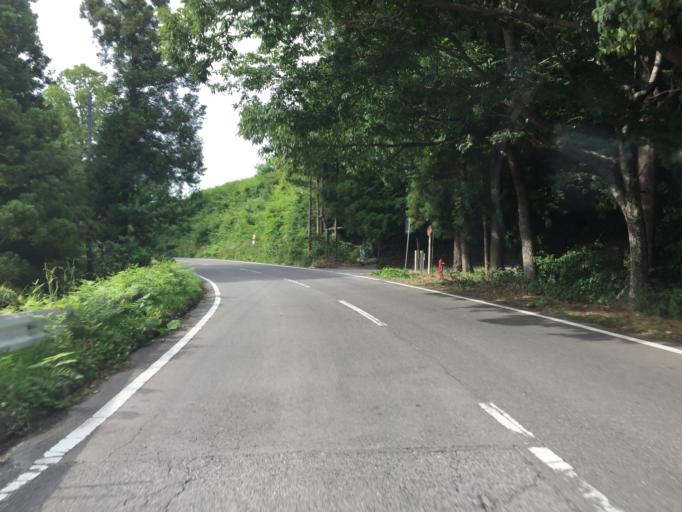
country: JP
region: Fukushima
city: Funehikimachi-funehiki
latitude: 37.5282
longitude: 140.5596
